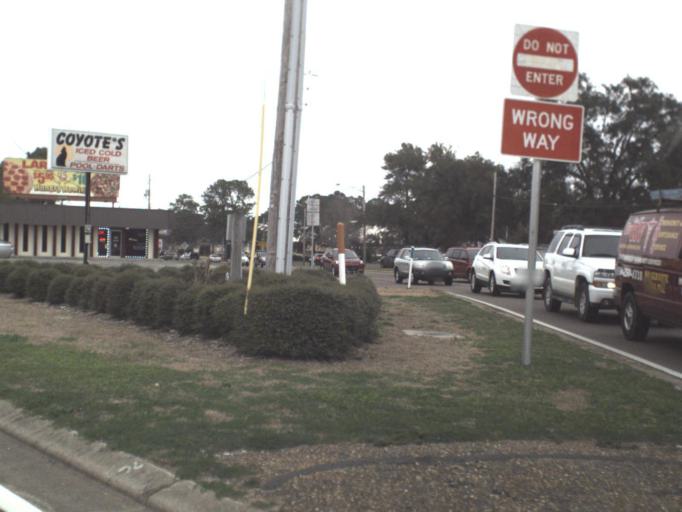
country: US
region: Florida
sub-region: Bay County
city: Parker
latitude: 30.1273
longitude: -85.5914
